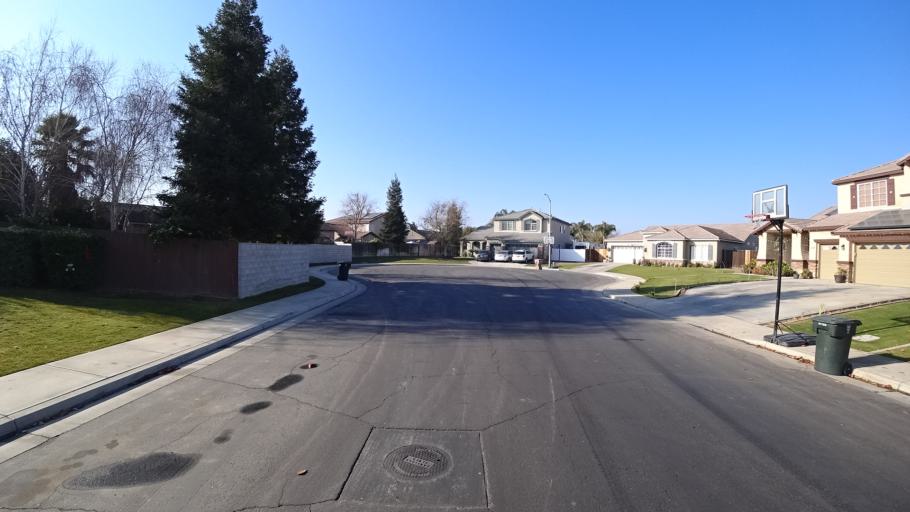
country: US
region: California
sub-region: Kern County
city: Greenacres
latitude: 35.3064
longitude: -119.1225
